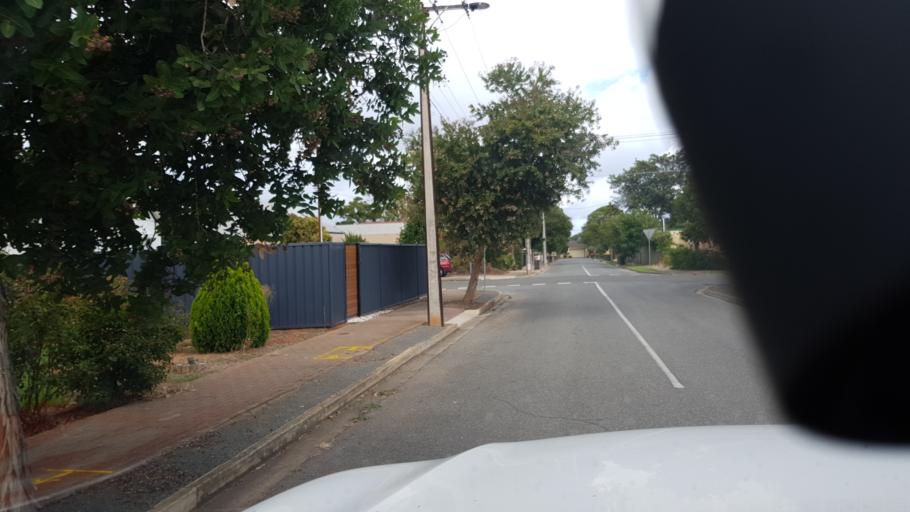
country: AU
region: South Australia
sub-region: Holdfast Bay
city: Seacliff Park
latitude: -35.0220
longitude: 138.5308
